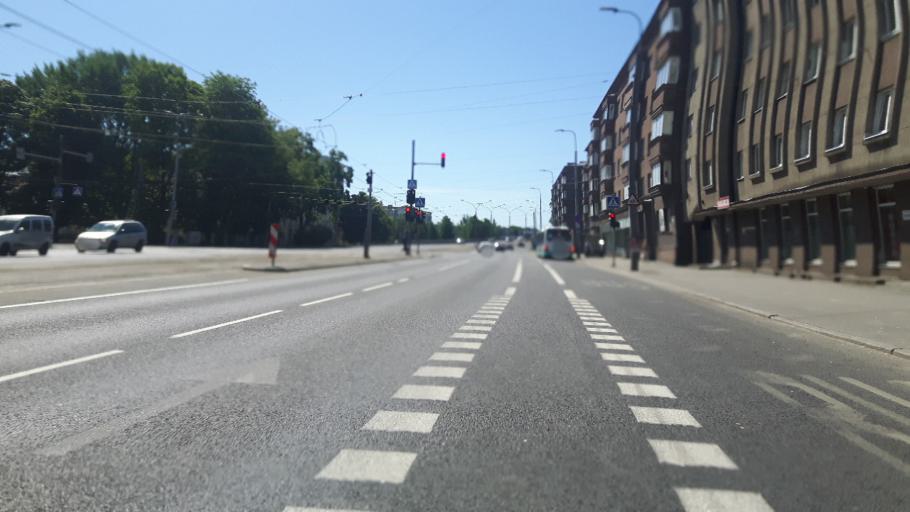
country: EE
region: Harju
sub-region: Tallinna linn
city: Tallinn
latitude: 59.4235
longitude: 24.7424
